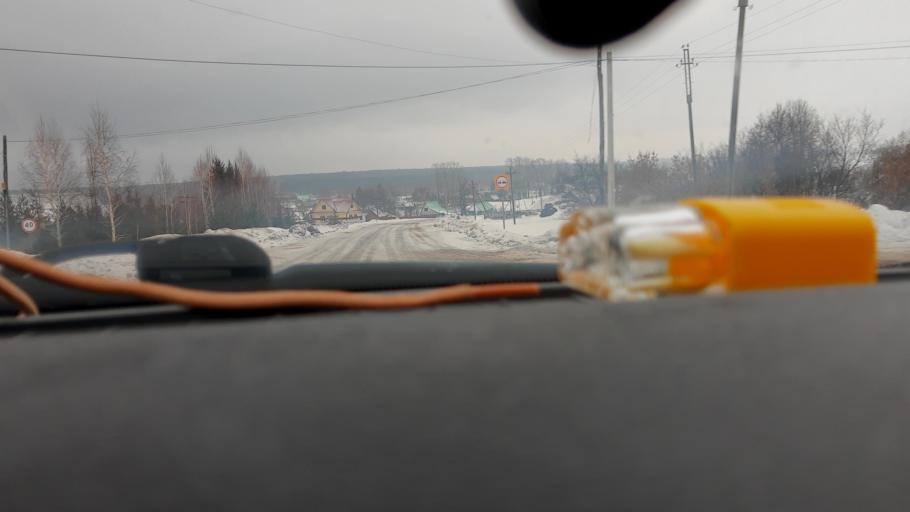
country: RU
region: Bashkortostan
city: Ulukulevo
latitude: 54.6091
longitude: 56.4247
